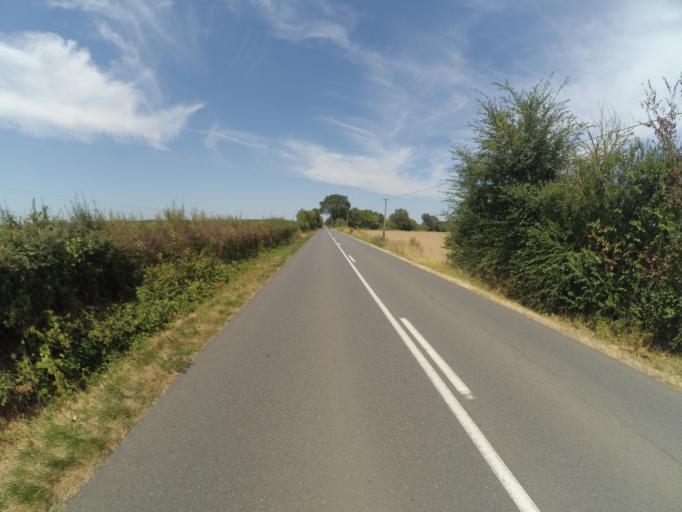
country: FR
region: Poitou-Charentes
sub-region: Departement de la Vienne
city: Usson-du-Poitou
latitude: 46.2577
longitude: 0.5231
